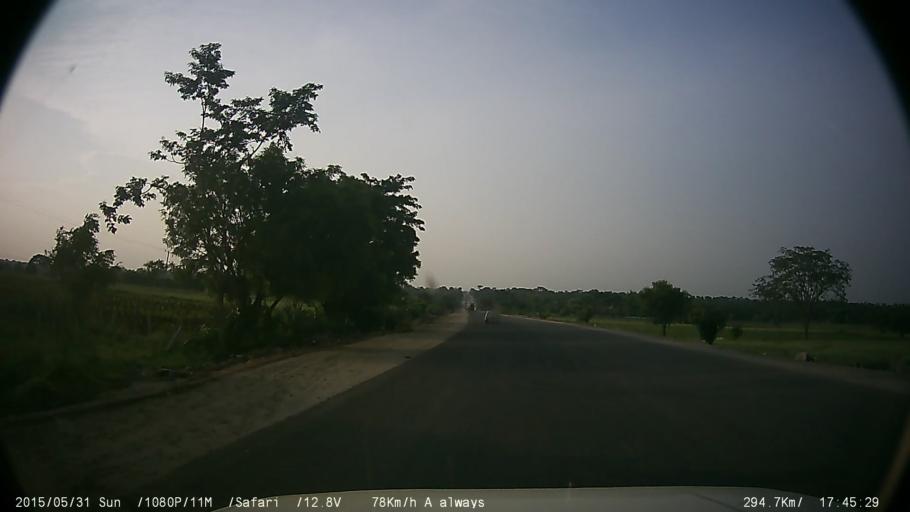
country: IN
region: Karnataka
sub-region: Chamrajnagar
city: Gundlupet
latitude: 11.9501
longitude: 76.6705
